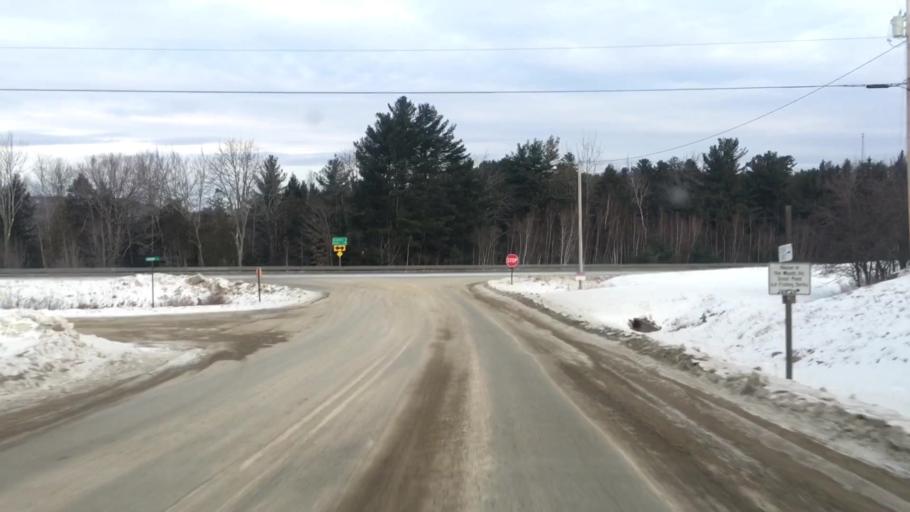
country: US
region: Maine
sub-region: Hancock County
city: Franklin
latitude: 44.8497
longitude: -68.3304
